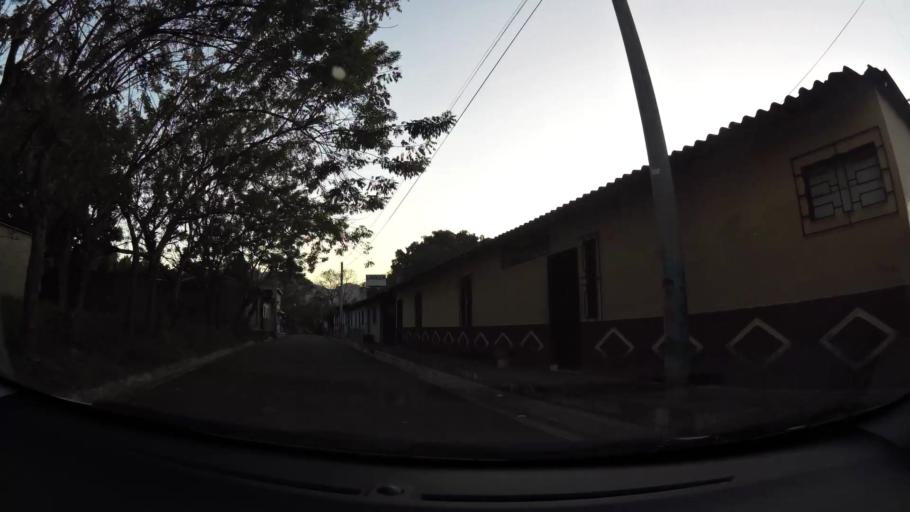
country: SV
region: Sonsonate
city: Armenia
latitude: 13.7343
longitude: -89.3833
